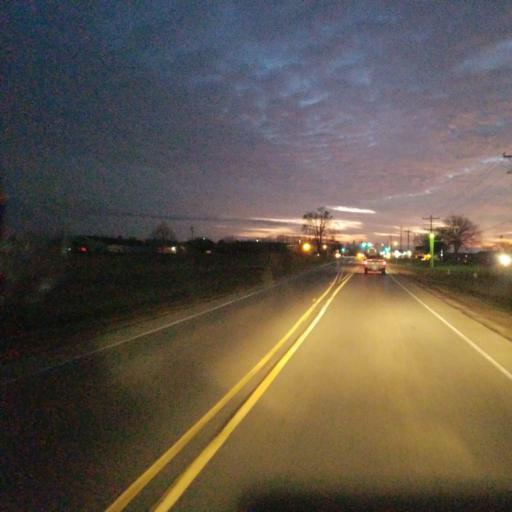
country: US
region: Illinois
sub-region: Peoria County
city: Bellevue
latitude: 40.6885
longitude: -89.6965
